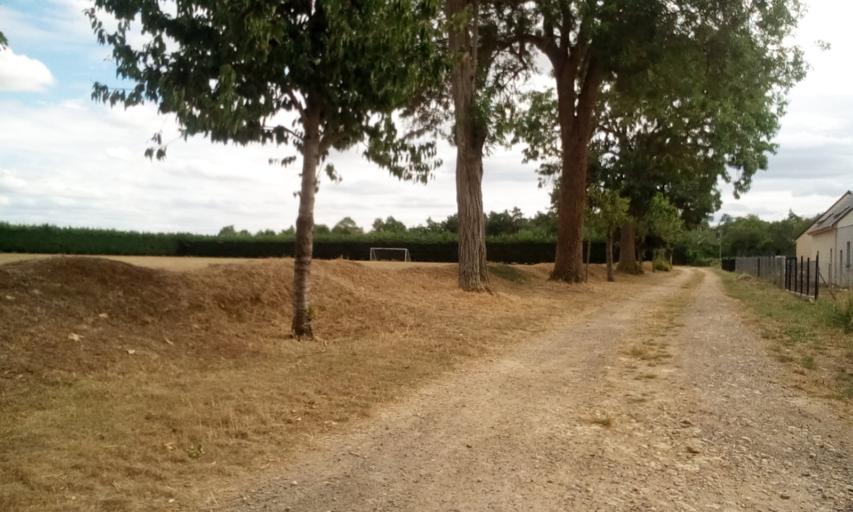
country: FR
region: Lower Normandy
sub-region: Departement du Calvados
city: Bellengreville
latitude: 49.1186
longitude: -0.2006
